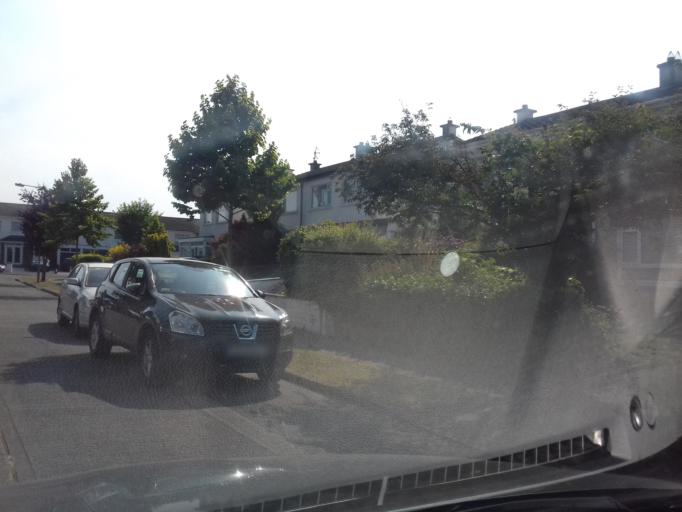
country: IE
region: Leinster
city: Malahide
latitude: 53.4533
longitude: -6.1669
